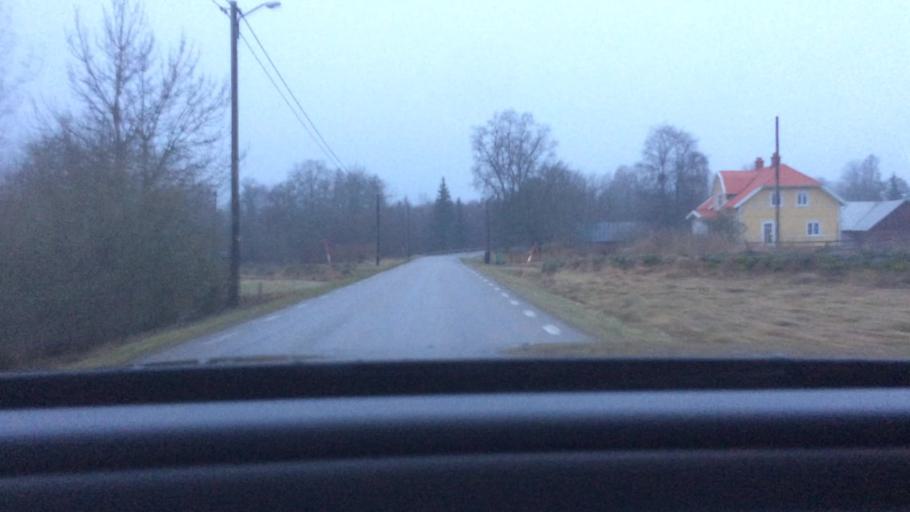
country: SE
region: Vaestra Goetaland
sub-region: Ulricehamns Kommun
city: Ulricehamn
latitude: 57.9537
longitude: 13.3876
